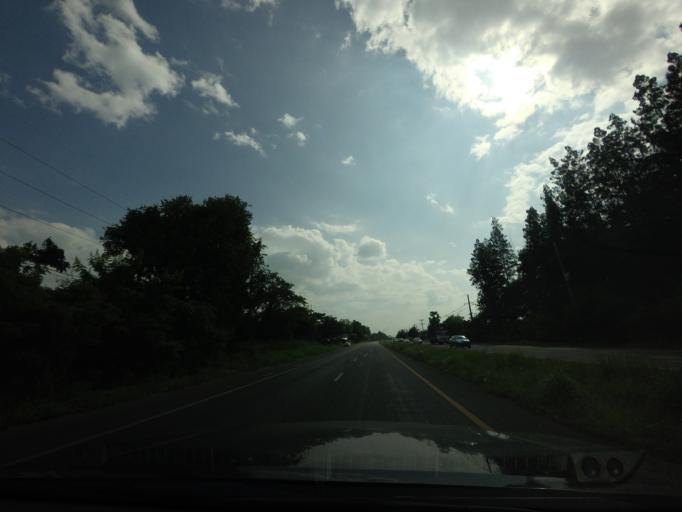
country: TH
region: Lop Buri
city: Chai Badan
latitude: 15.1891
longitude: 101.0782
